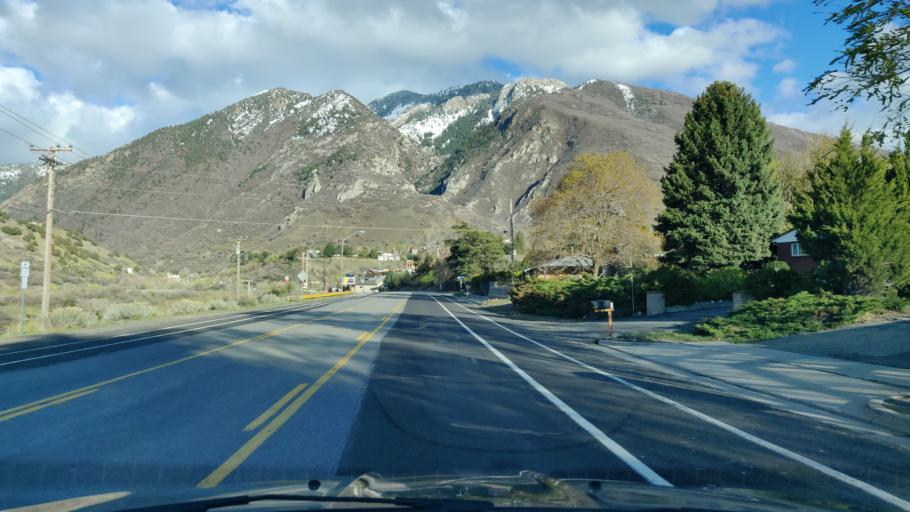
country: US
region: Utah
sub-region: Salt Lake County
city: Cottonwood Heights
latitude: 40.6206
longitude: -111.7956
